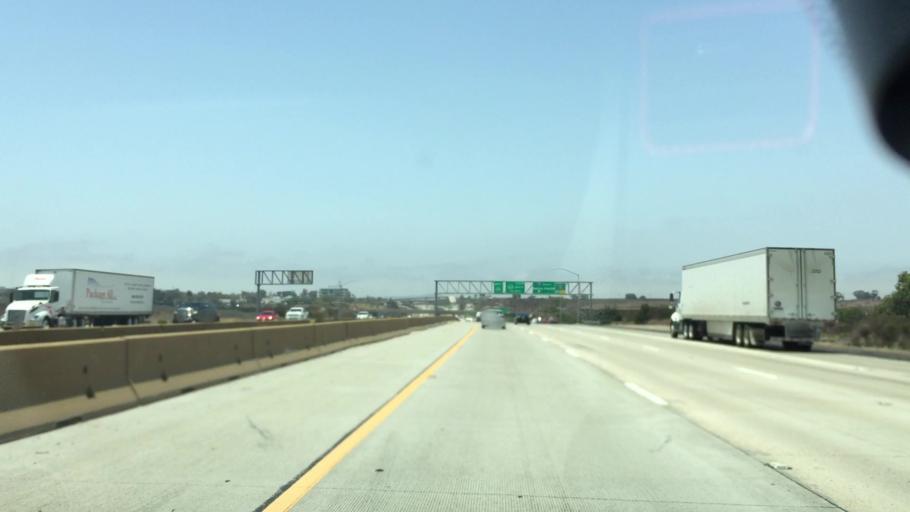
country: US
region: California
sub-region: San Diego County
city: La Mesa
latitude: 32.8420
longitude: -117.1118
